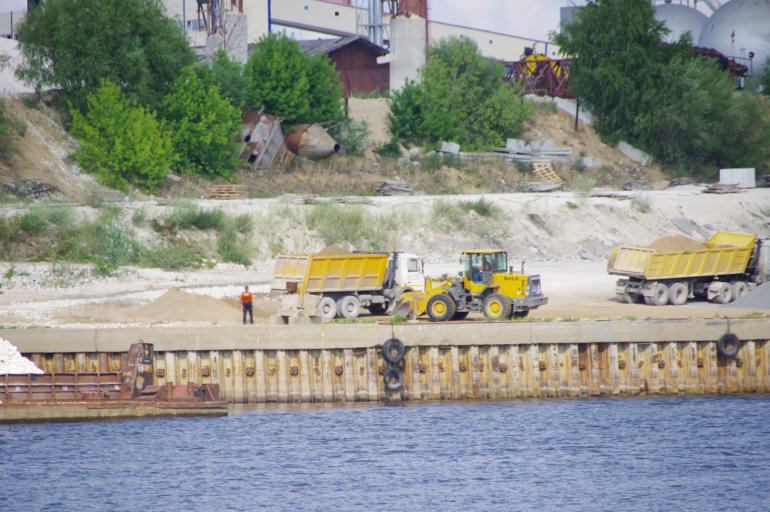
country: RU
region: Nizjnij Novgorod
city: Bor
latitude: 56.3365
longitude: 44.0783
